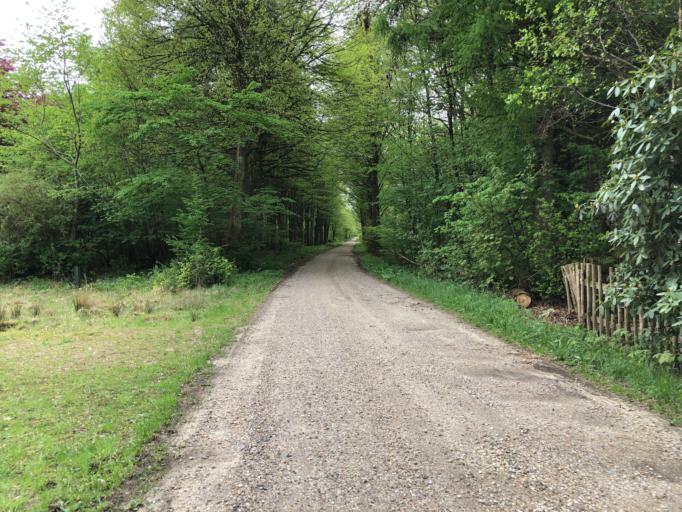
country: DK
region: Central Jutland
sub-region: Holstebro Kommune
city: Ulfborg
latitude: 56.2746
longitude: 8.4324
